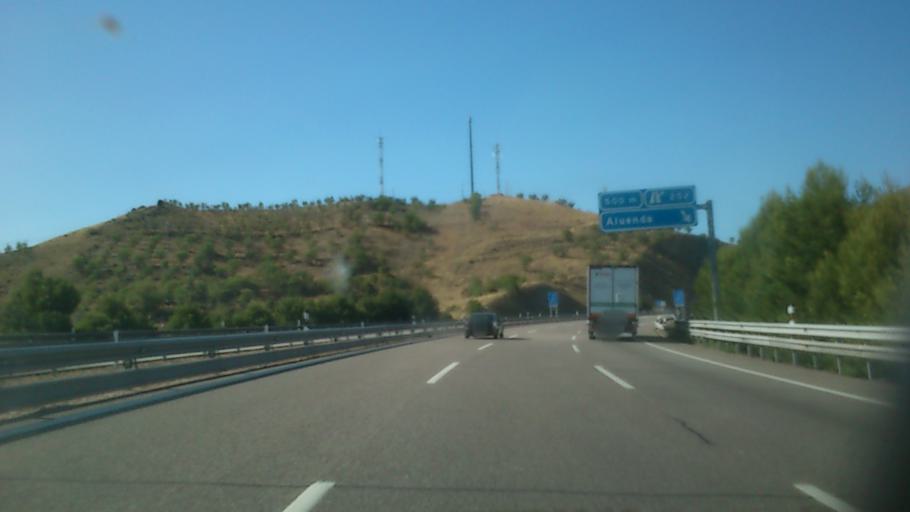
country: ES
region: Aragon
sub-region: Provincia de Zaragoza
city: Paracuellos de la Ribera
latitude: 41.4093
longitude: -1.5269
